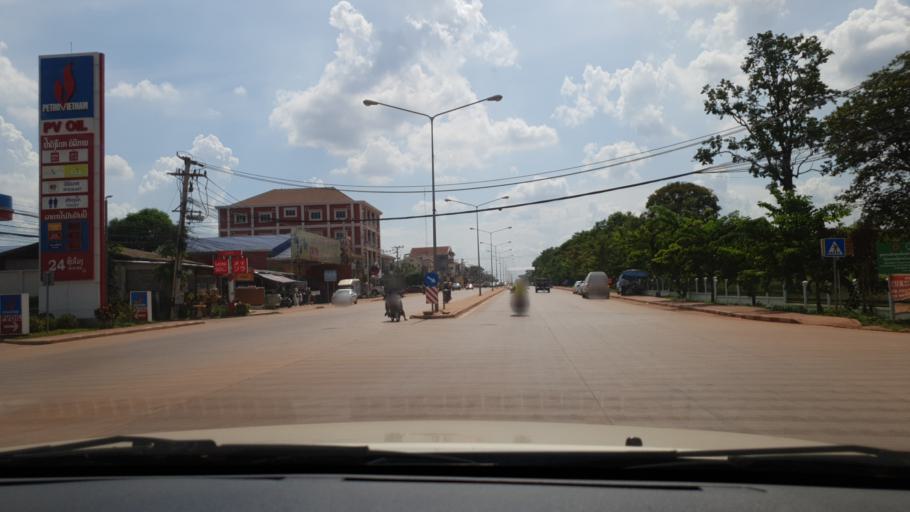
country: LA
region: Vientiane
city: Vientiane
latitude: 18.0329
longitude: 102.6405
